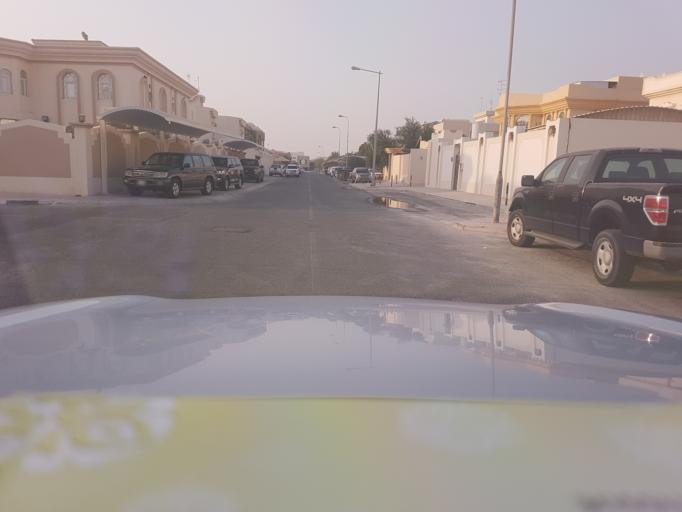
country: QA
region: Baladiyat ad Dawhah
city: Doha
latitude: 25.2344
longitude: 51.5646
